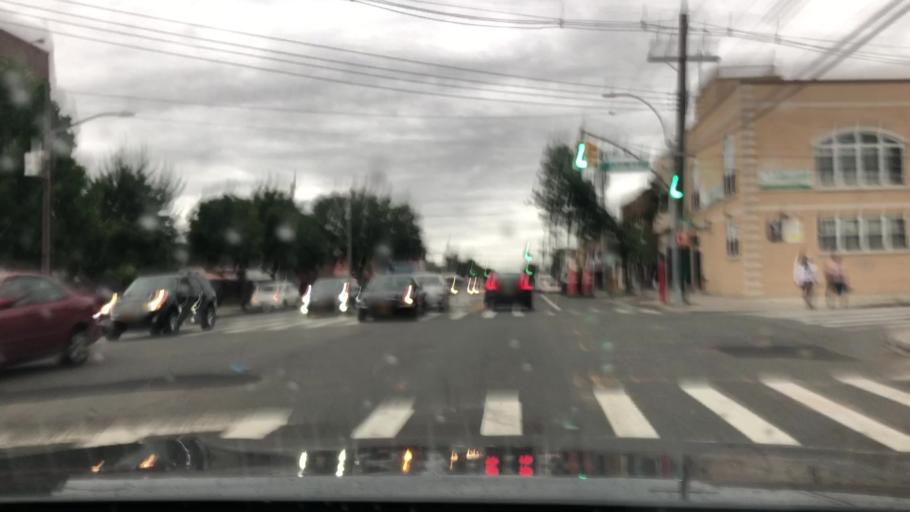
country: US
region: New York
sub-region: Queens County
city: Jamaica
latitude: 40.6750
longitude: -73.8087
